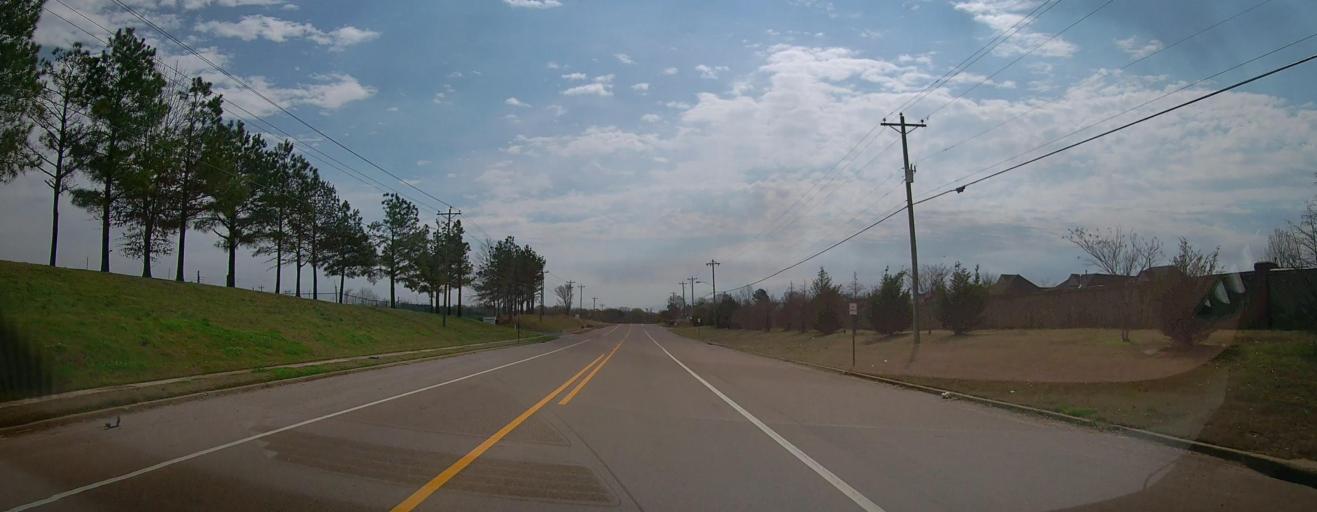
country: US
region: Mississippi
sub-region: De Soto County
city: Olive Branch
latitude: 34.9786
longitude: -89.8517
